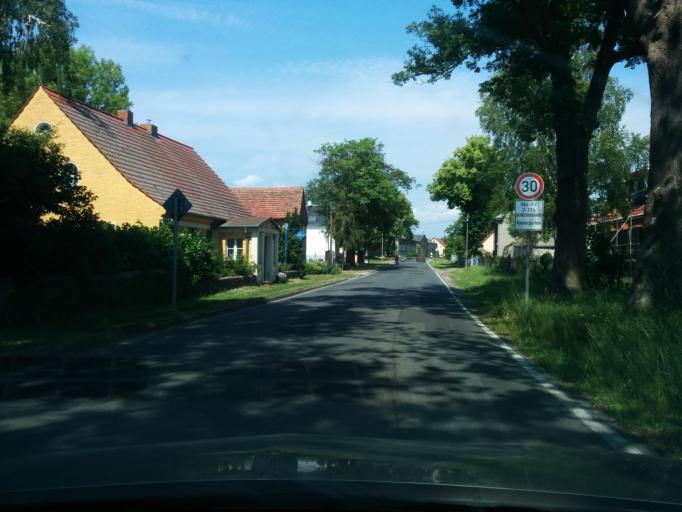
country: DE
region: Brandenburg
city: Ahrensfelde
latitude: 52.6237
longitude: 13.5758
